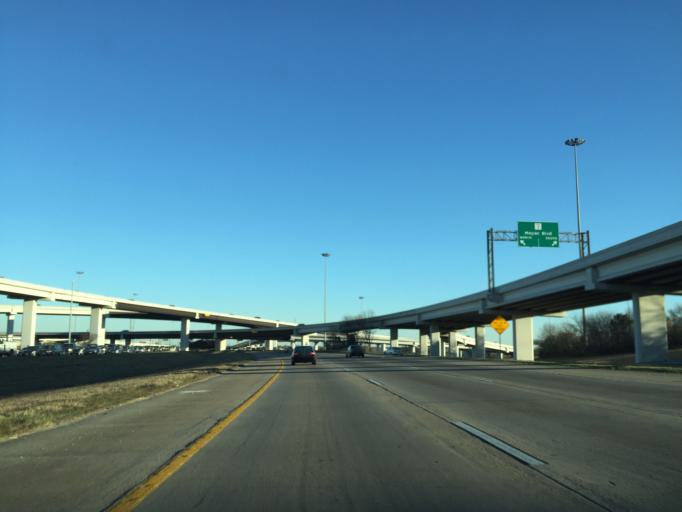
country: US
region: Texas
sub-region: Williamson County
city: Jollyville
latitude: 30.3812
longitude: -97.7405
